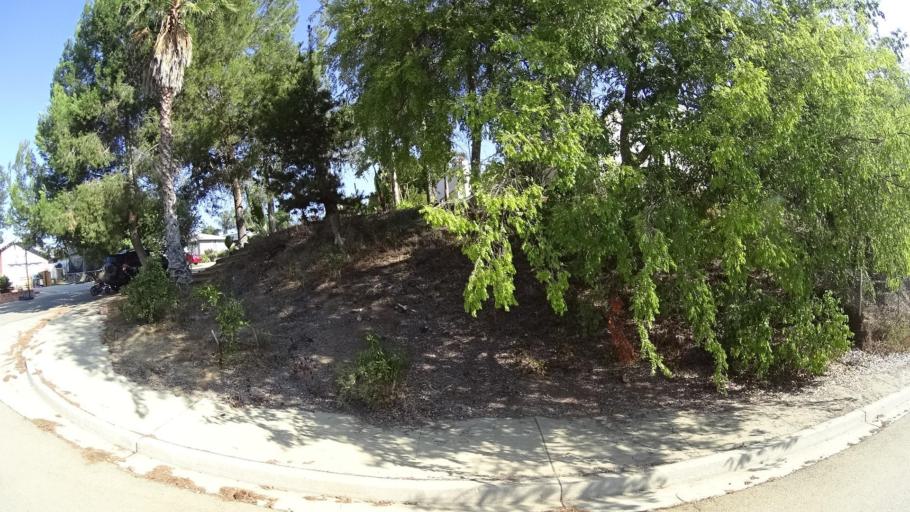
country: US
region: California
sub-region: San Diego County
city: Fallbrook
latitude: 33.3729
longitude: -117.2320
